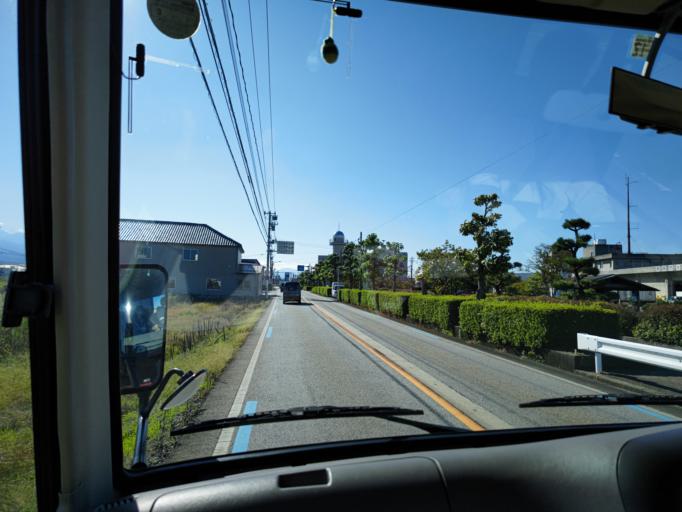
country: JP
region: Toyama
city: Nyuzen
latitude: 36.8933
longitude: 137.4195
